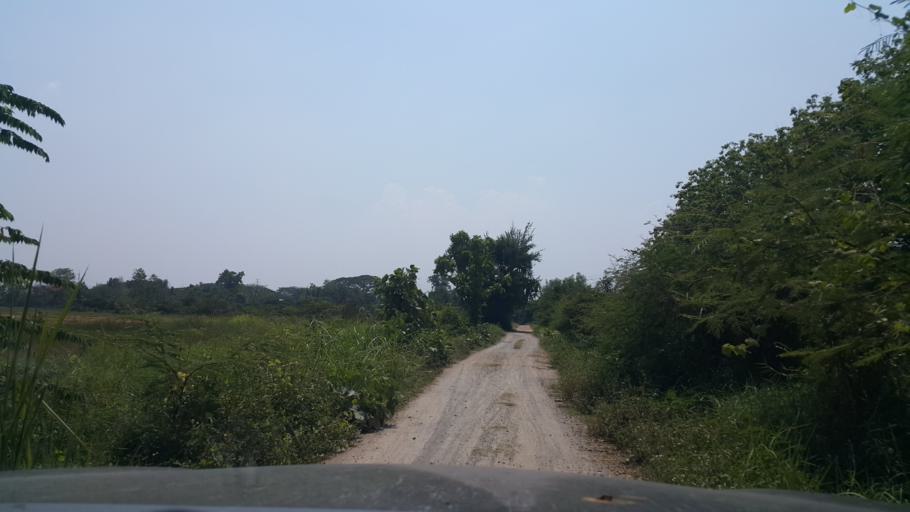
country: TH
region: Chiang Mai
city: Saraphi
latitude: 18.7215
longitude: 98.9771
